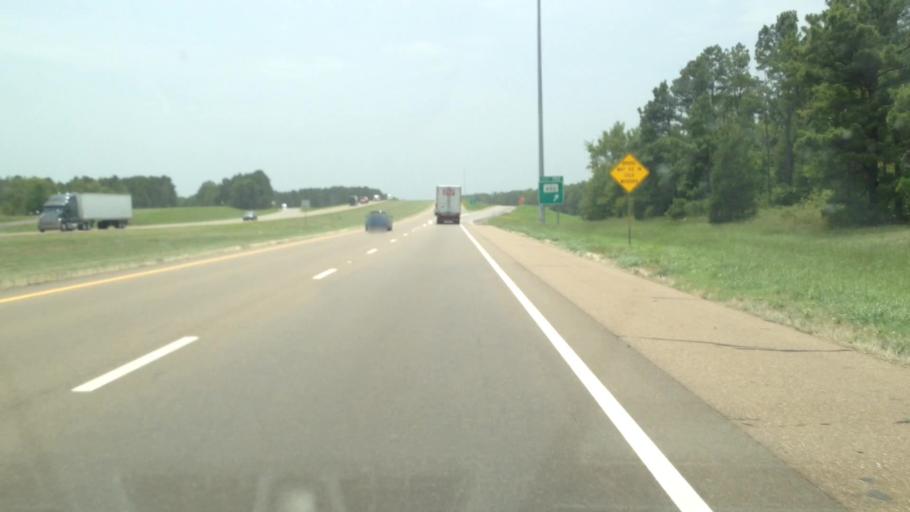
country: US
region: Texas
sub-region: Bowie County
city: De Kalb
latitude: 33.4196
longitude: -94.5527
